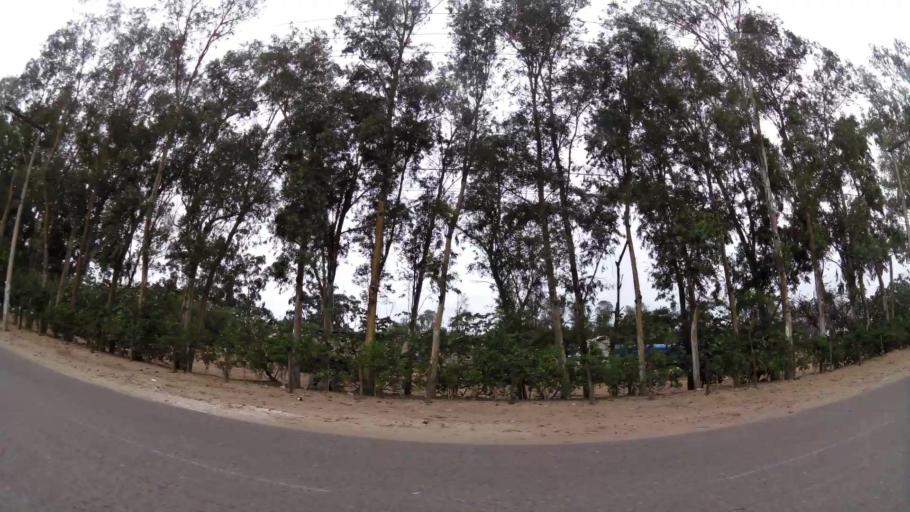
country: BO
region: Santa Cruz
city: Santa Cruz de la Sierra
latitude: -17.8142
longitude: -63.1643
